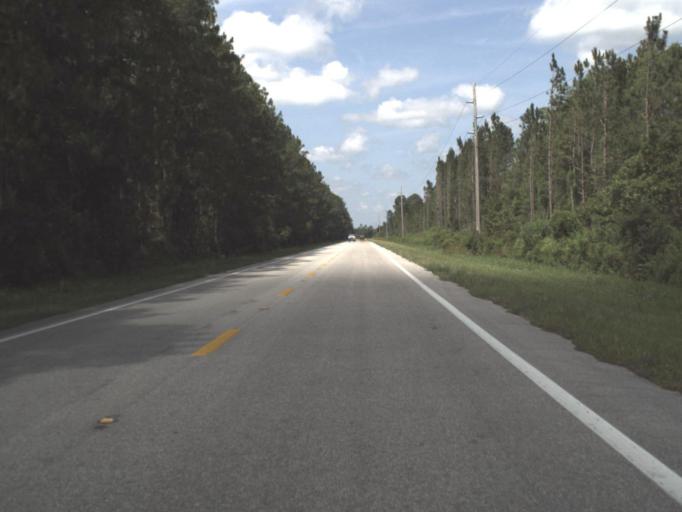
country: US
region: Florida
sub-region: Levy County
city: Bronson
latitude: 29.4295
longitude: -82.6639
